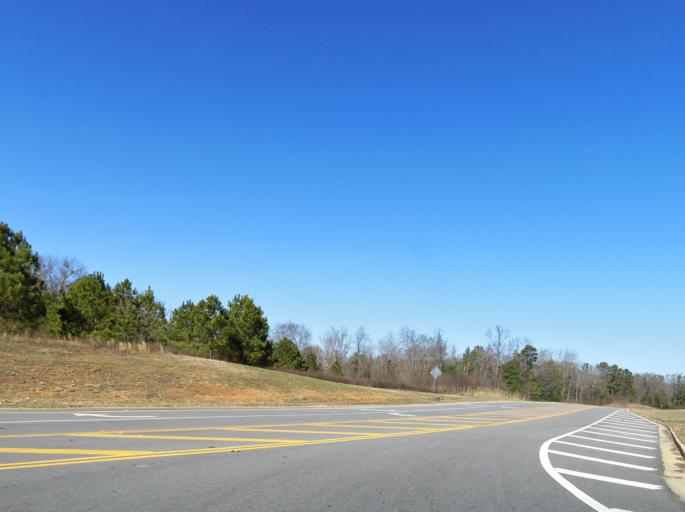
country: US
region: Georgia
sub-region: Peach County
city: Byron
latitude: 32.7169
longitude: -83.7348
